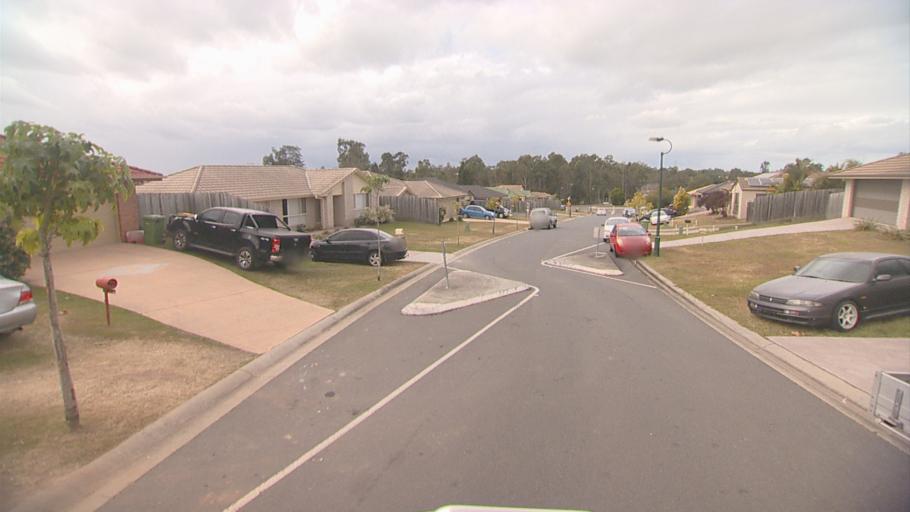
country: AU
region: Queensland
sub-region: Logan
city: Park Ridge South
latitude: -27.6845
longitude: 153.0473
